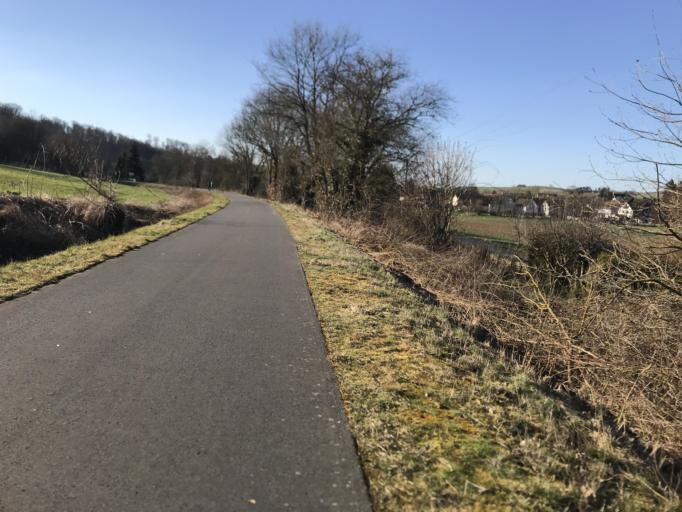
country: DE
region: Hesse
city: Neukirchen
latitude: 50.8720
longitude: 9.3307
